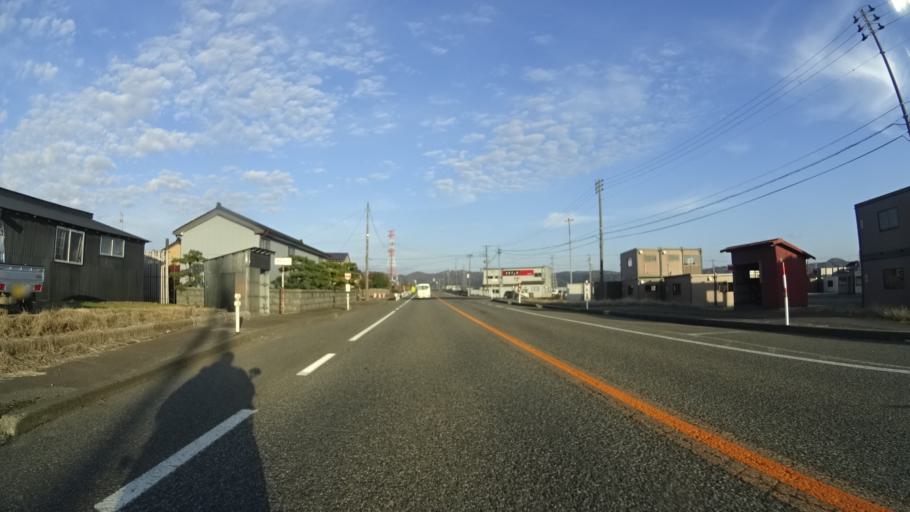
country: JP
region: Niigata
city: Kashiwazaki
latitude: 37.3987
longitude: 138.6090
